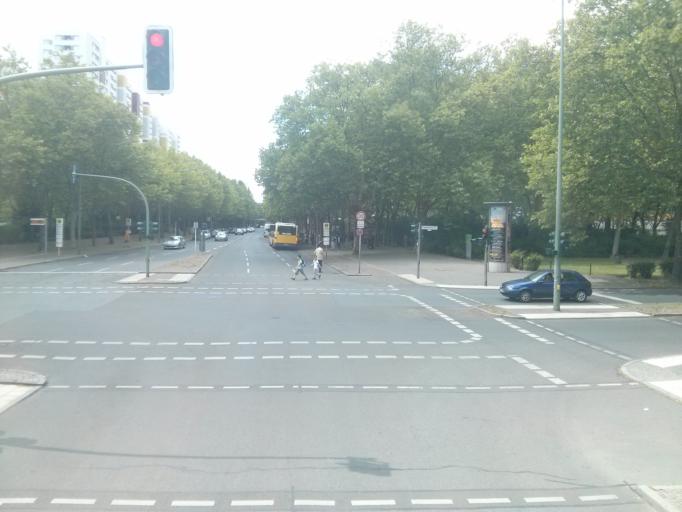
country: DE
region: Berlin
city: Markisches Viertel
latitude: 52.5970
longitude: 13.3609
